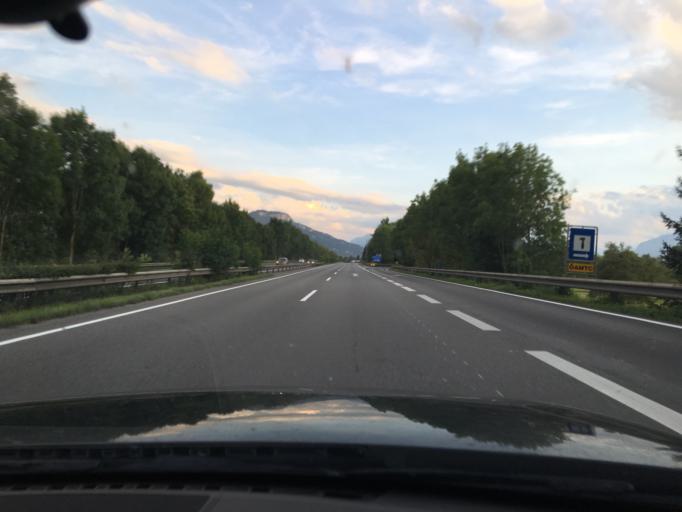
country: AT
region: Vorarlberg
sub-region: Politischer Bezirk Dornbirn
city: Dornbirn
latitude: 47.4168
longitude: 9.7097
